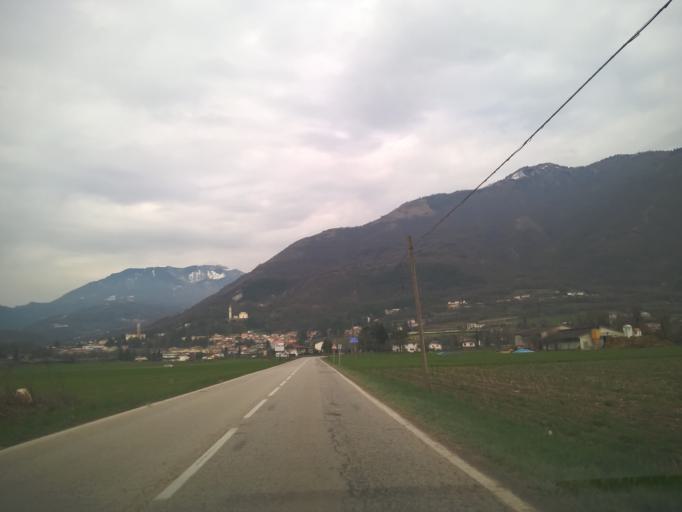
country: IT
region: Veneto
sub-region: Provincia di Vicenza
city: Santorso
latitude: 45.7317
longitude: 11.4106
